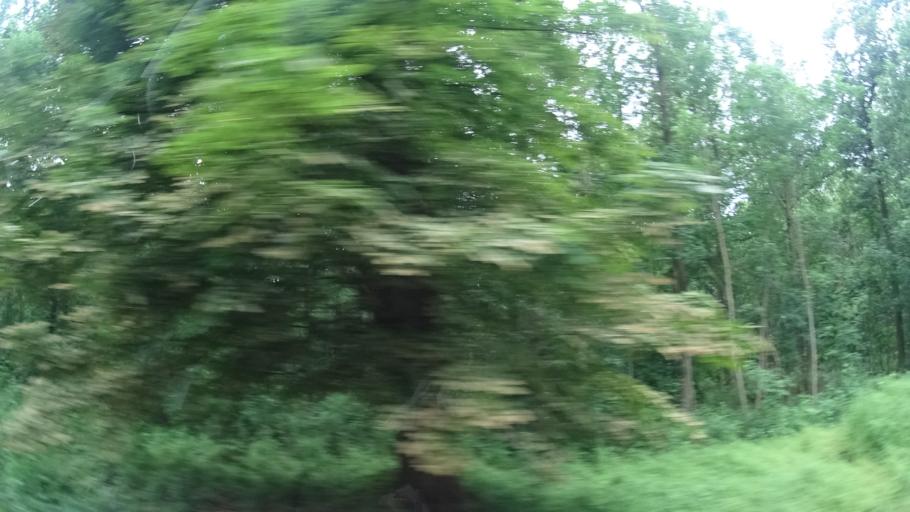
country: DE
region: Lower Saxony
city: Springe
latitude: 52.1808
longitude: 9.5927
